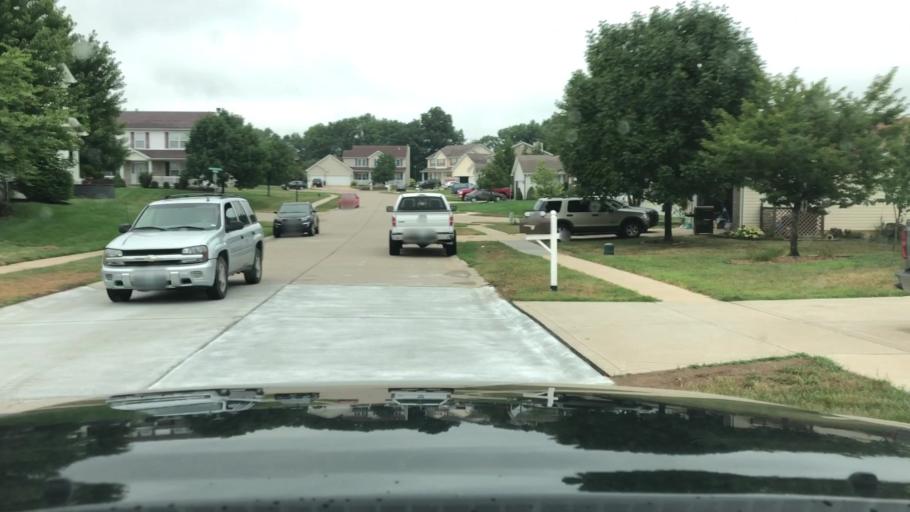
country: US
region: Missouri
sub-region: Saint Charles County
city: Wentzville
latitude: 38.8376
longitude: -90.8835
